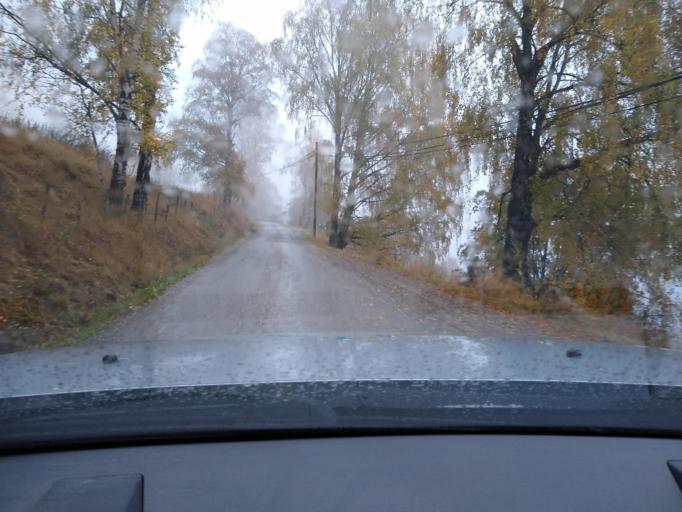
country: NO
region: Oppland
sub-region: Ringebu
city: Ringebu
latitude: 61.5306
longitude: 10.1507
